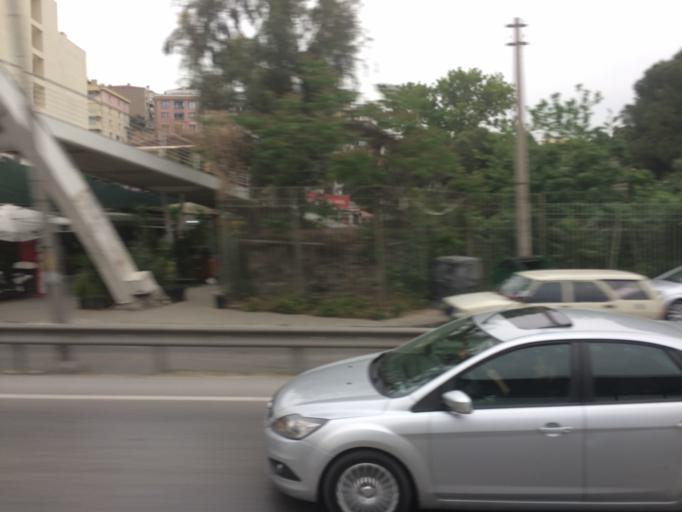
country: TR
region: Izmir
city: Karsiyaka
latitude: 38.4636
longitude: 27.1632
